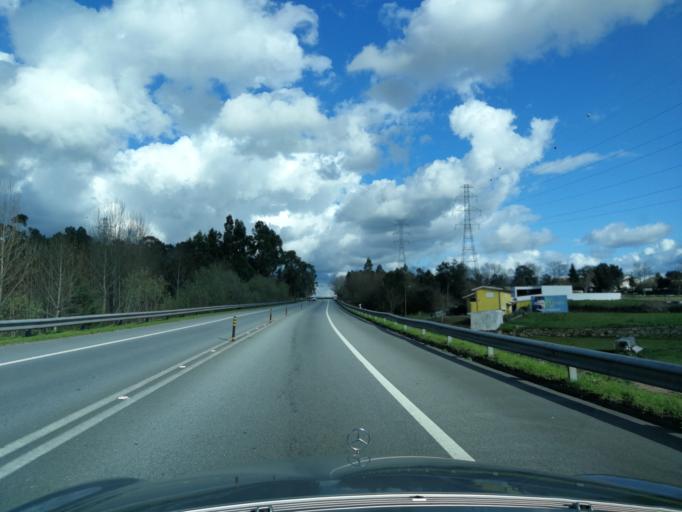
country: PT
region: Braga
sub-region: Vila Verde
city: Prado
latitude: 41.6171
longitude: -8.4456
